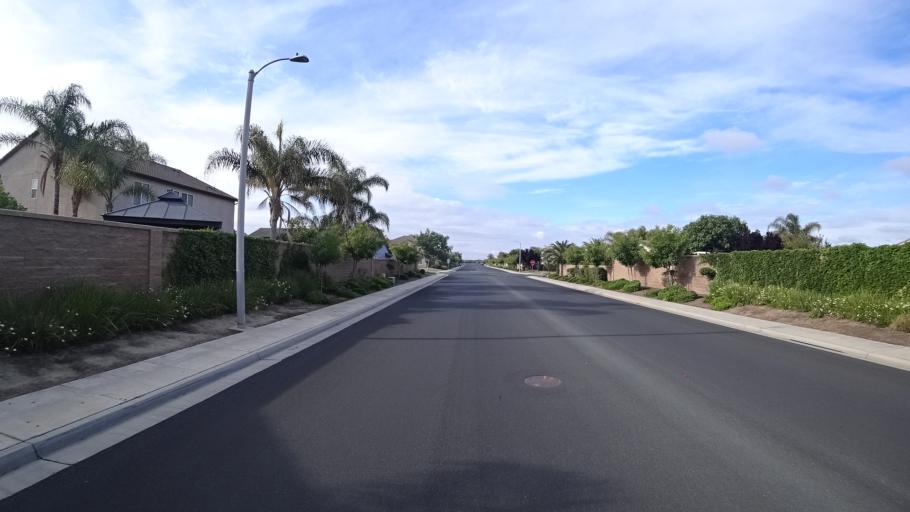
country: US
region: California
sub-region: Kings County
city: Lucerne
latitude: 36.3463
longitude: -119.6783
